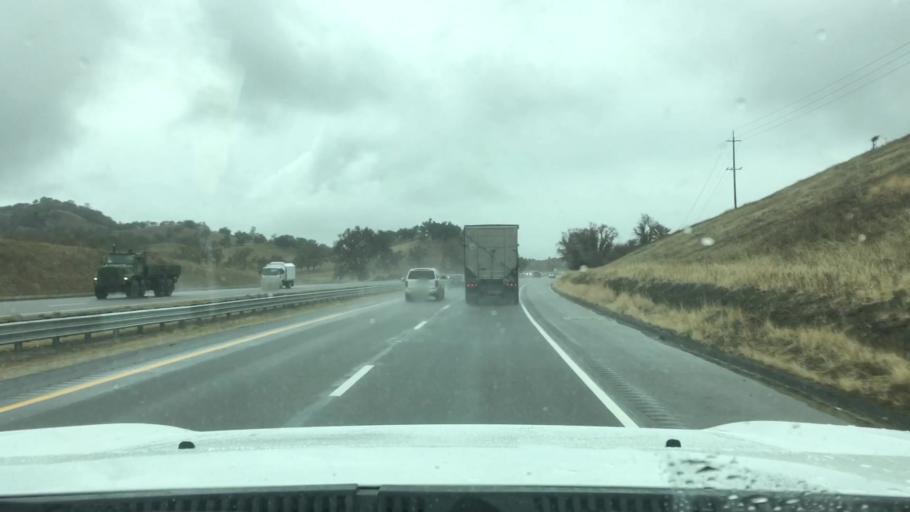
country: US
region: California
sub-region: San Luis Obispo County
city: Santa Margarita
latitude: 35.4079
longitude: -120.6256
